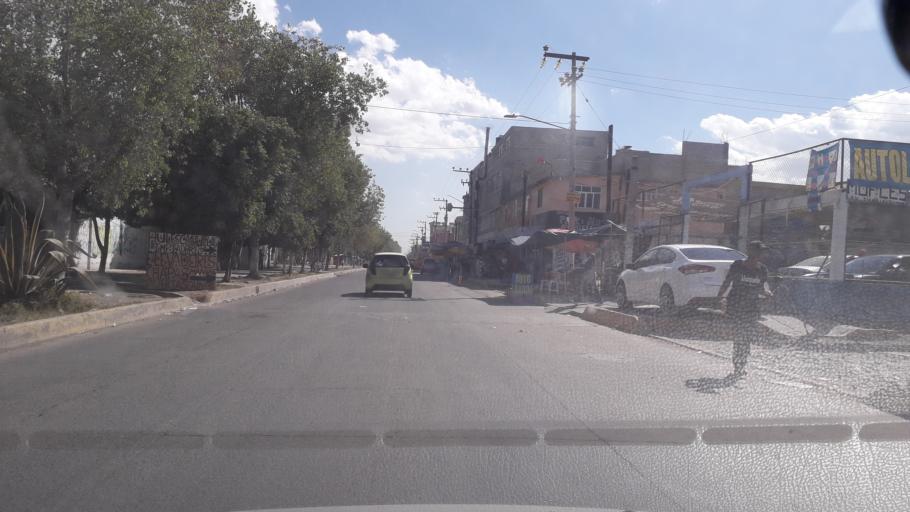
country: MX
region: Mexico
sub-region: Jaltenco
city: Alborada Jaltenco
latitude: 19.6522
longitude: -99.0656
